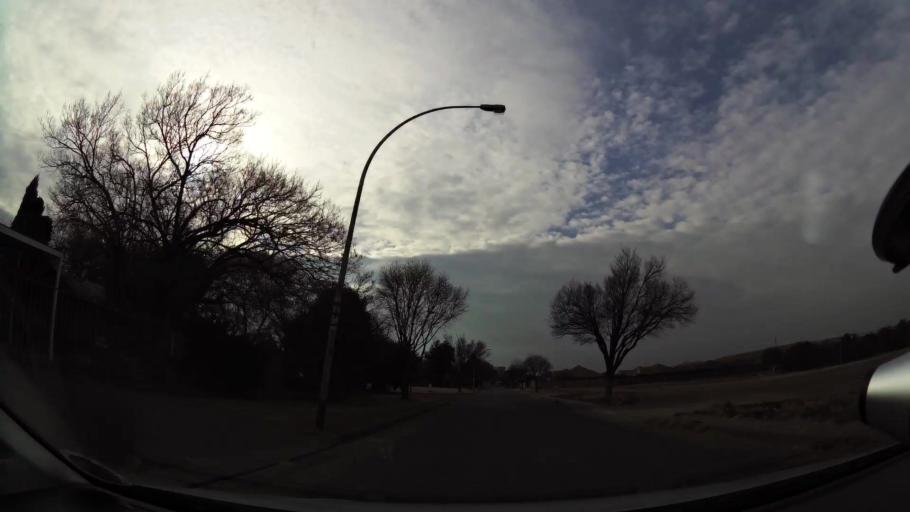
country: ZA
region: Orange Free State
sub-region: Mangaung Metropolitan Municipality
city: Bloemfontein
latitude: -29.1202
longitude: 26.1859
